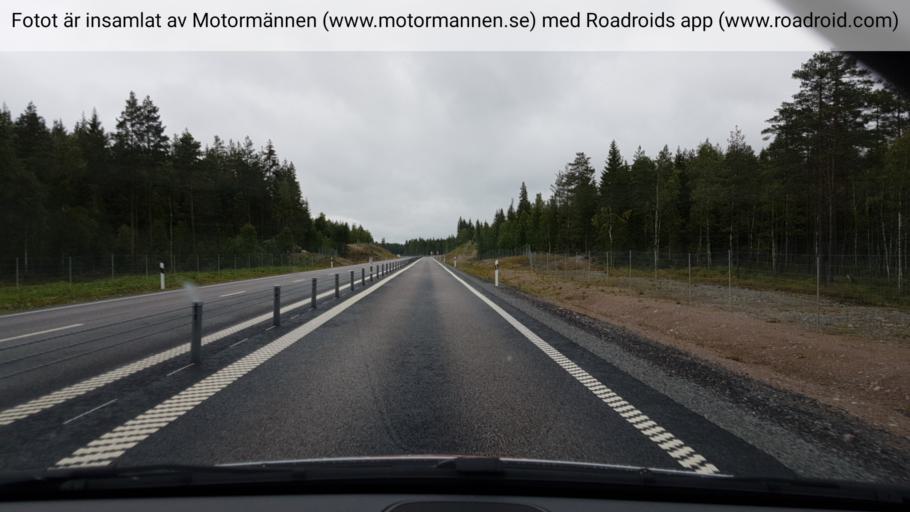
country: SE
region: Uppsala
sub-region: Heby Kommun
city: Tarnsjo
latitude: 60.1116
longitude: 16.9222
